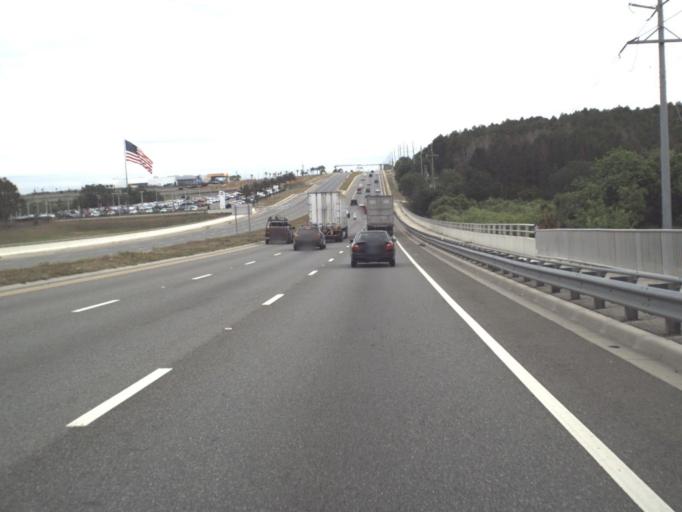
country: US
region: Florida
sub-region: Orange County
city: Oakland
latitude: 28.5463
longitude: -81.6796
